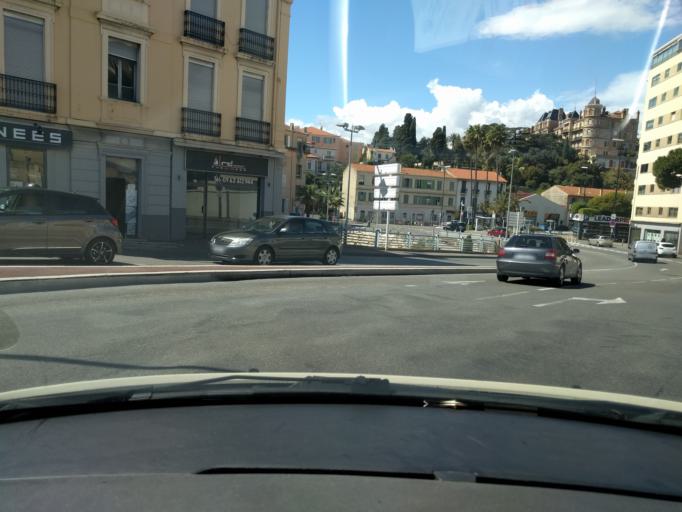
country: FR
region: Provence-Alpes-Cote d'Azur
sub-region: Departement des Alpes-Maritimes
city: Cannes
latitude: 43.5509
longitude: 7.0075
